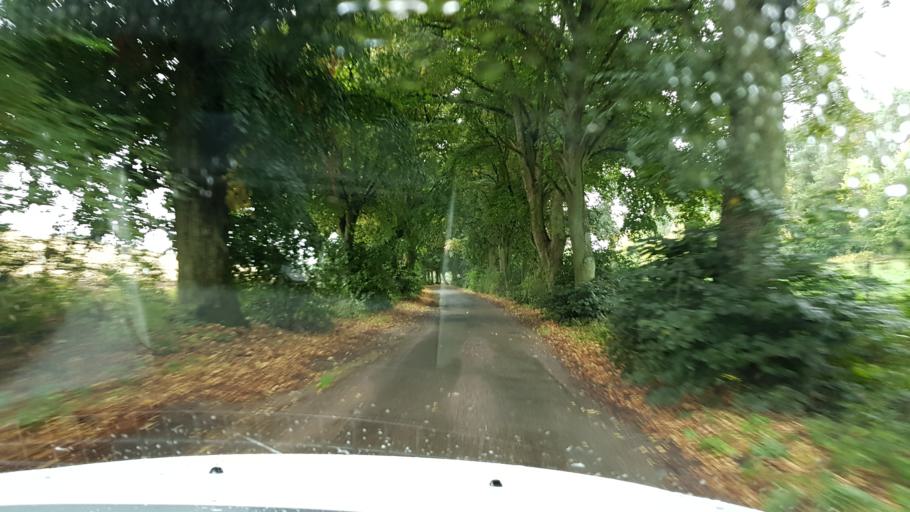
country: DE
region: Brandenburg
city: Meyenburg
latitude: 52.9922
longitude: 14.2750
